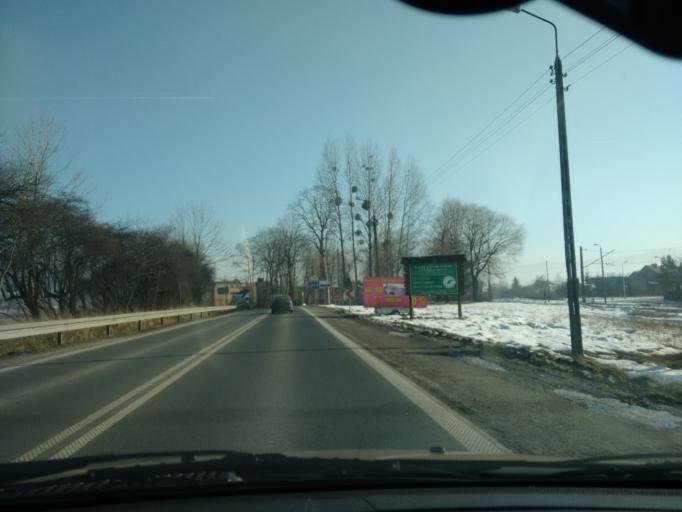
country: PL
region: Lesser Poland Voivodeship
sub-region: Powiat wadowicki
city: Roczyny
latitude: 49.8585
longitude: 19.3248
